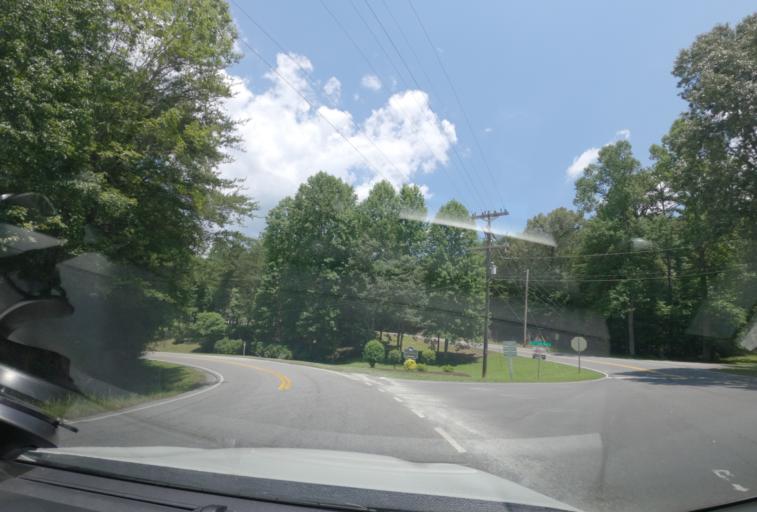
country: US
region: South Carolina
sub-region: Pickens County
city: Pickens
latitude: 34.9661
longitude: -82.8629
